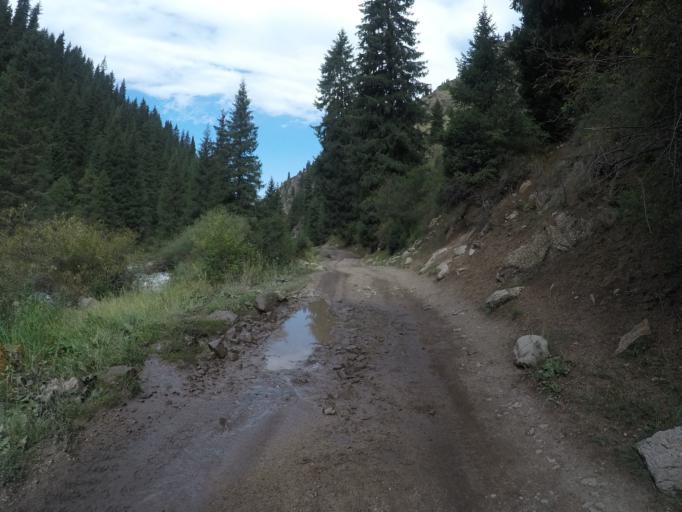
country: KG
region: Ysyk-Koel
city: Teploklyuchenka
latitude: 42.4410
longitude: 78.5564
